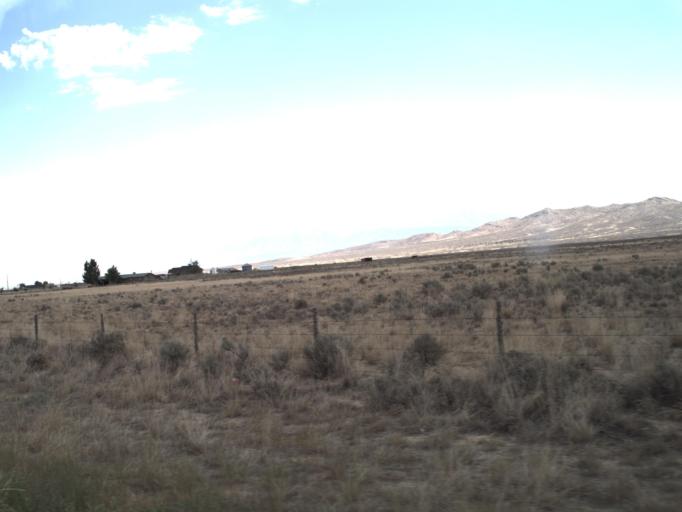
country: US
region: Utah
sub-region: Tooele County
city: Tooele
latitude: 40.0872
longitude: -112.4287
